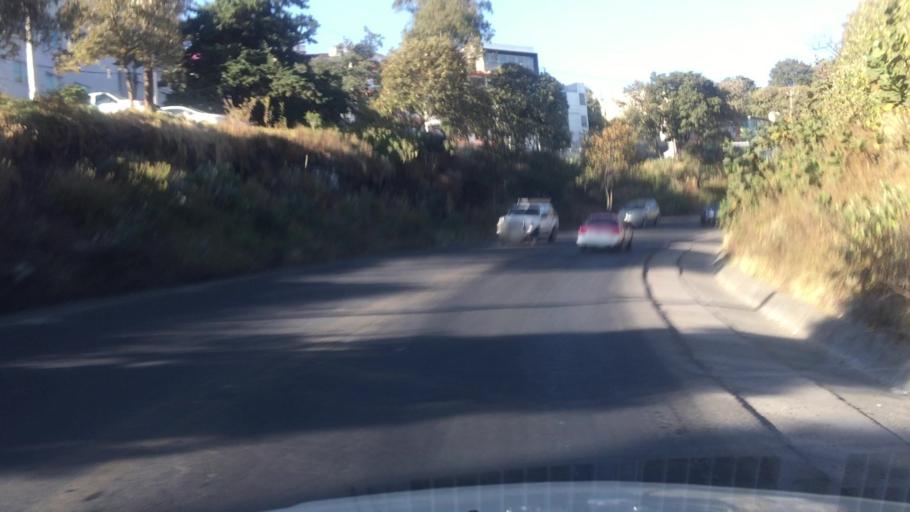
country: MX
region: Mexico City
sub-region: Tlalpan
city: Lomas de Tepemecatl
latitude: 19.2654
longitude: -99.2053
